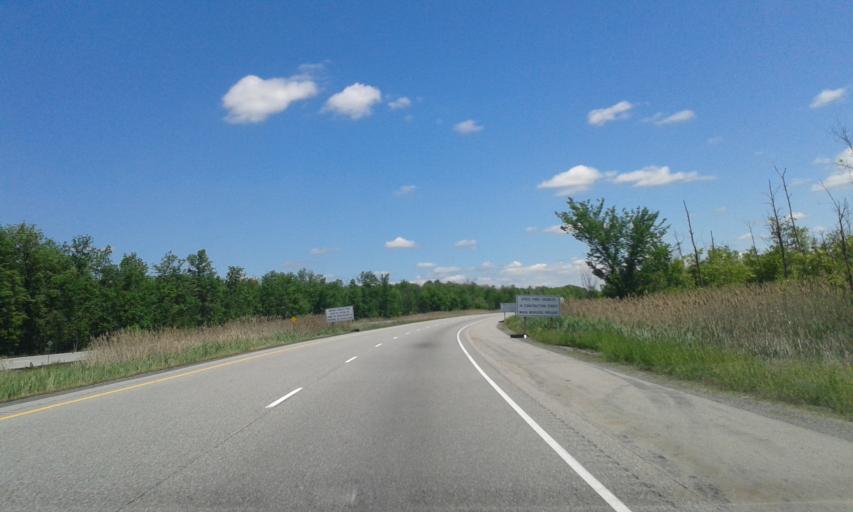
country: US
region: New York
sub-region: St. Lawrence County
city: Massena
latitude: 44.9789
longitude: -75.0765
